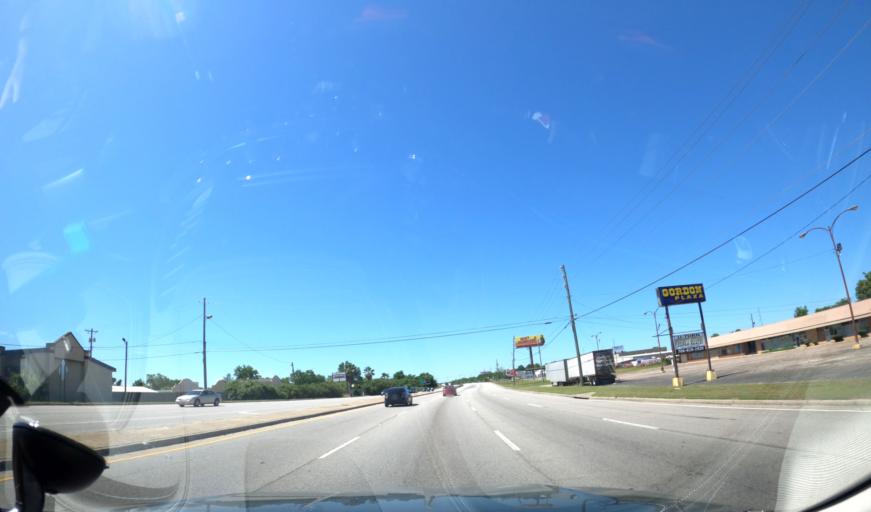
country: US
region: Georgia
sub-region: Richmond County
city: Augusta
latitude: 33.4551
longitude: -81.9694
